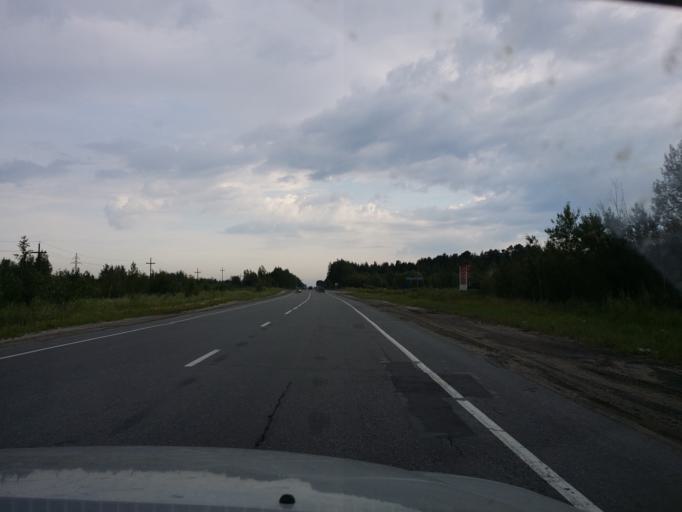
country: RU
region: Khanty-Mansiyskiy Avtonomnyy Okrug
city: Megion
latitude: 61.0595
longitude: 76.1144
